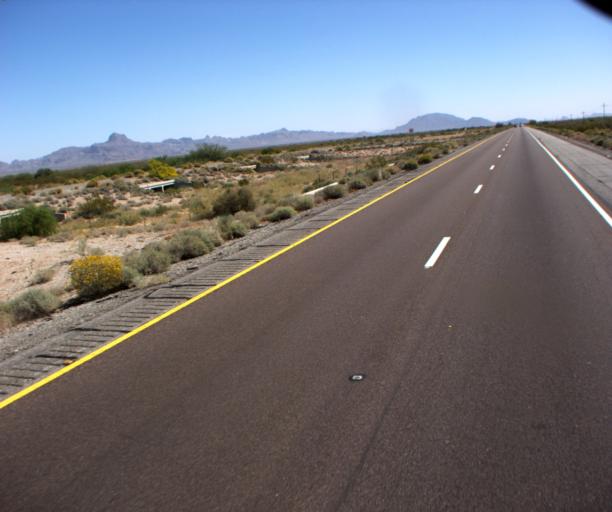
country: US
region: Arizona
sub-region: La Paz County
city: Salome
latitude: 33.5572
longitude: -113.2774
